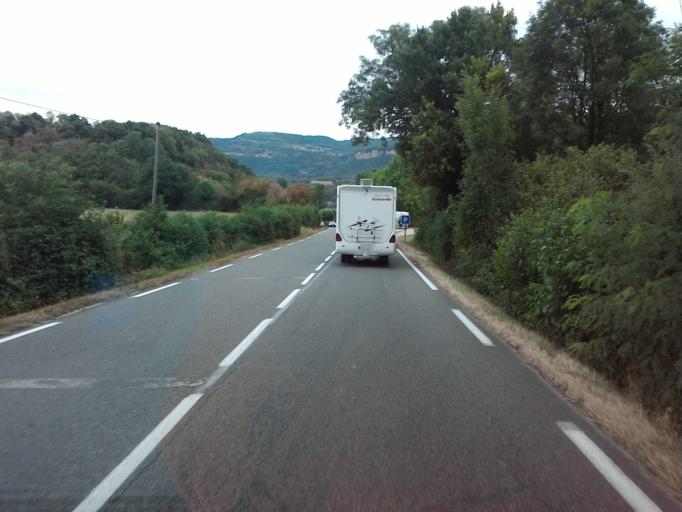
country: FR
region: Rhone-Alpes
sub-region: Departement de l'Ain
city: Sault-Brenaz
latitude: 45.8399
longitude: 5.4155
